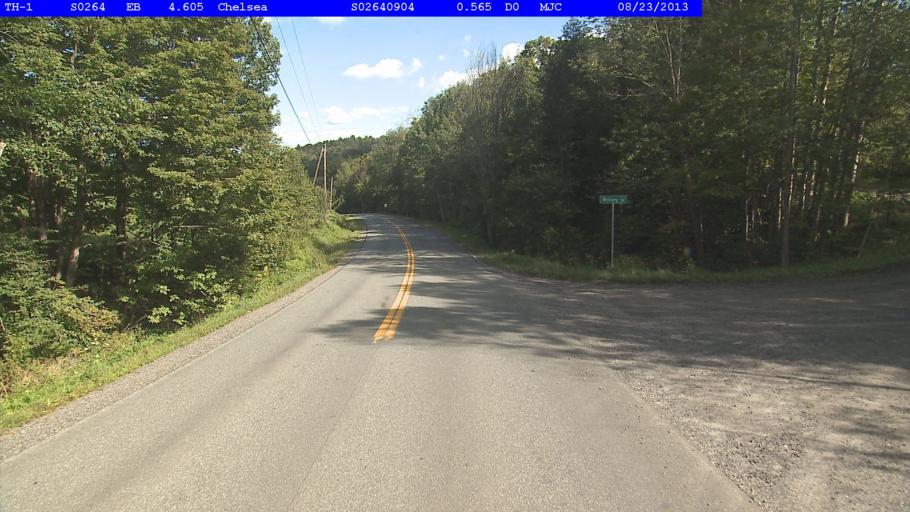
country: US
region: Vermont
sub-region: Orange County
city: Chelsea
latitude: 43.9720
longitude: -72.5017
